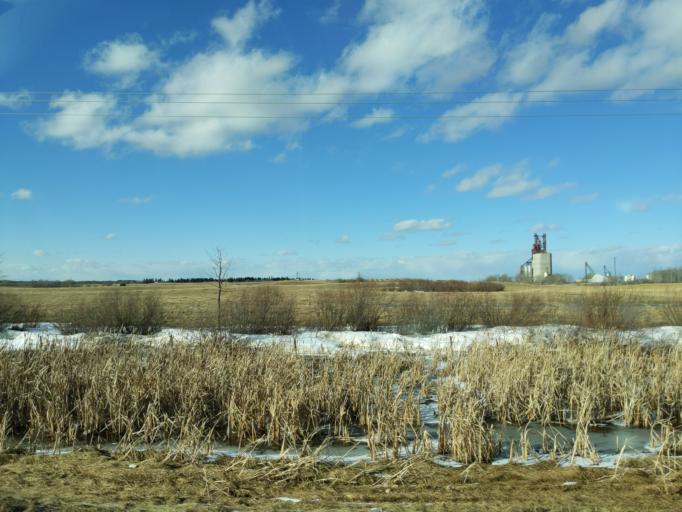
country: CA
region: Saskatchewan
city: Lloydminster
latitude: 53.2489
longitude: -109.9695
